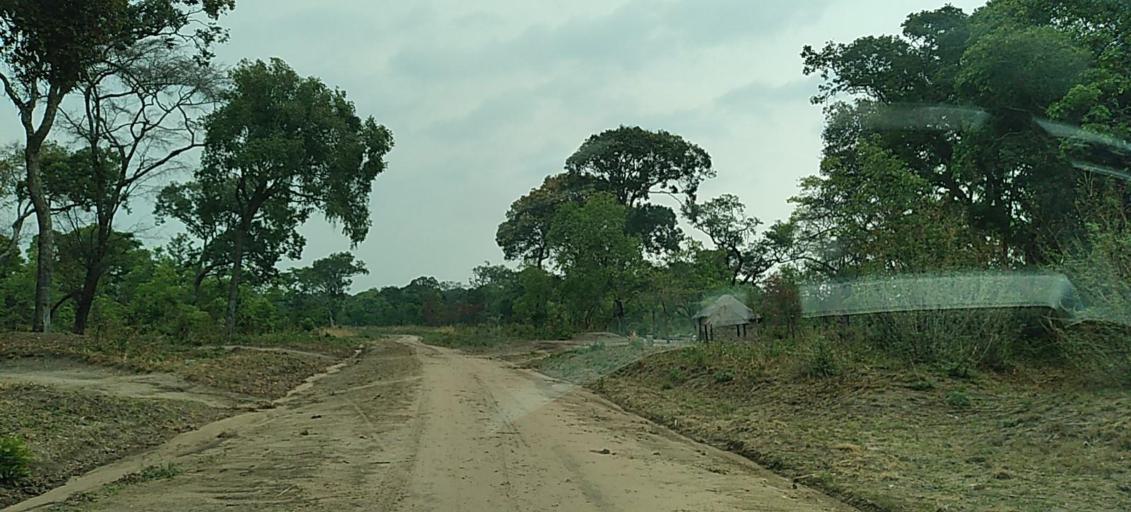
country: ZM
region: North-Western
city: Mwinilunga
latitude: -11.4214
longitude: 24.5958
